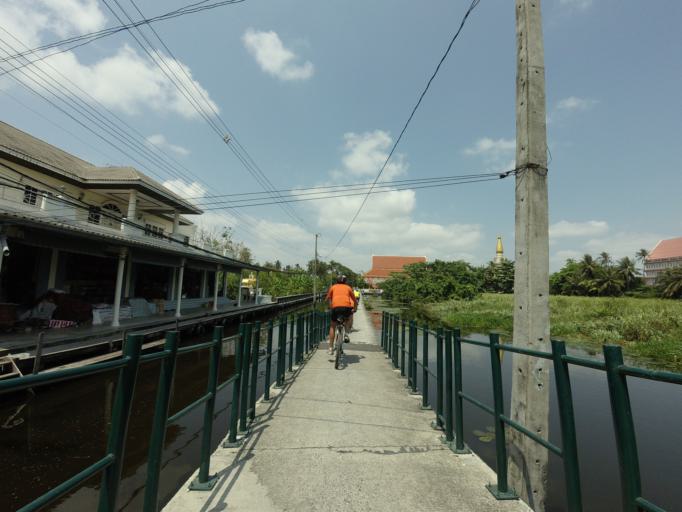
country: TH
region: Bangkok
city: Chom Thong
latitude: 13.6481
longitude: 100.4725
